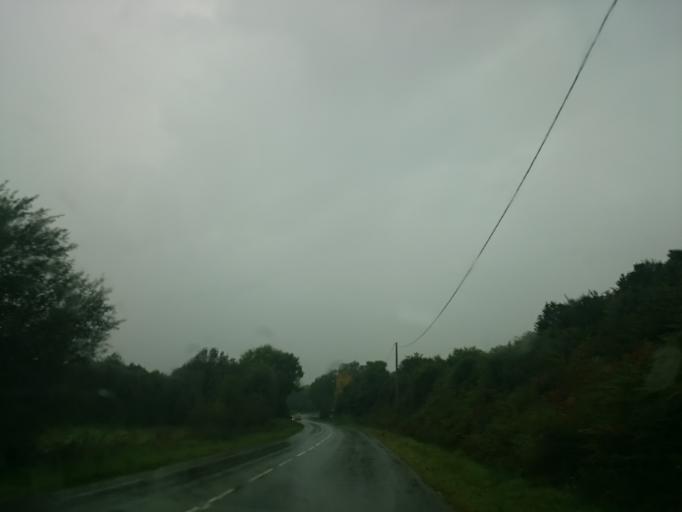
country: FR
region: Brittany
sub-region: Departement du Finistere
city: Plouvien
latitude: 48.5366
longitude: -4.4789
